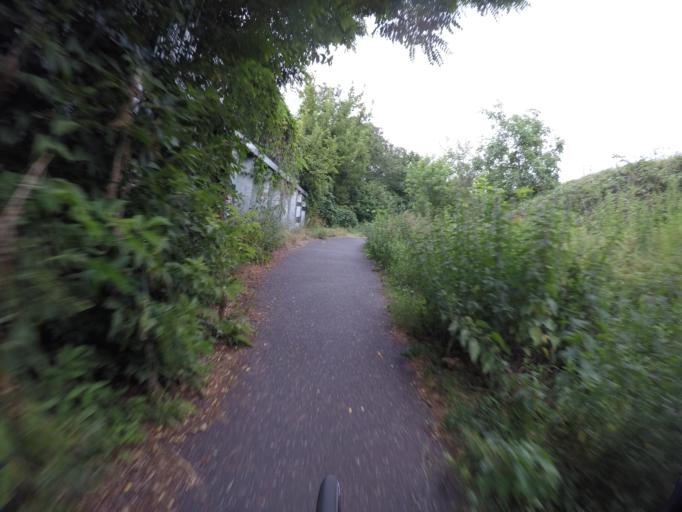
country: DE
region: Berlin
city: Markisches Viertel
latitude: 52.5897
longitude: 13.3482
